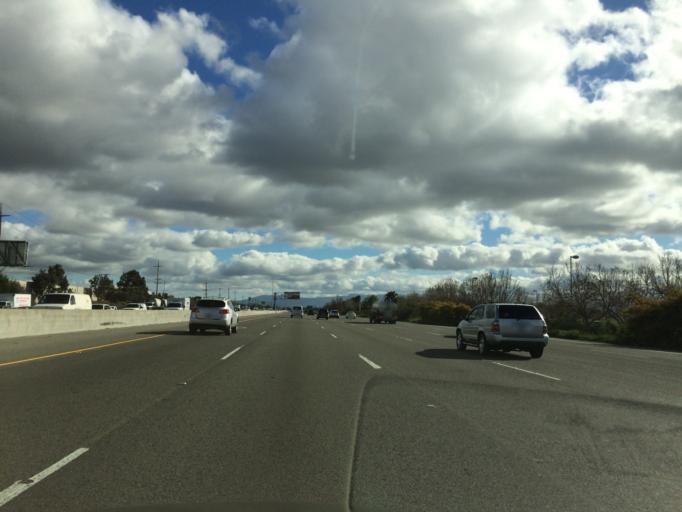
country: US
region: California
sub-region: Santa Clara County
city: Milpitas
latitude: 37.4455
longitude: -121.9213
